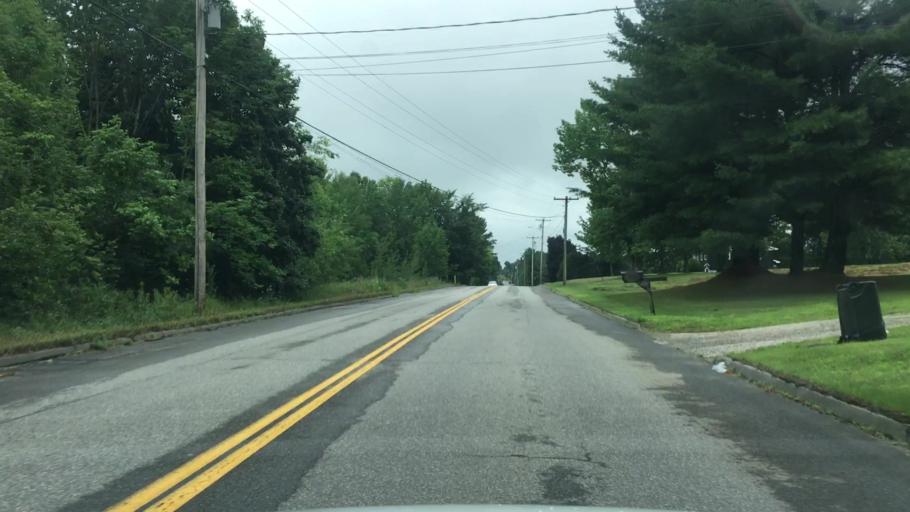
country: US
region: Maine
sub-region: Kennebec County
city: Augusta
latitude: 44.3162
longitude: -69.7377
